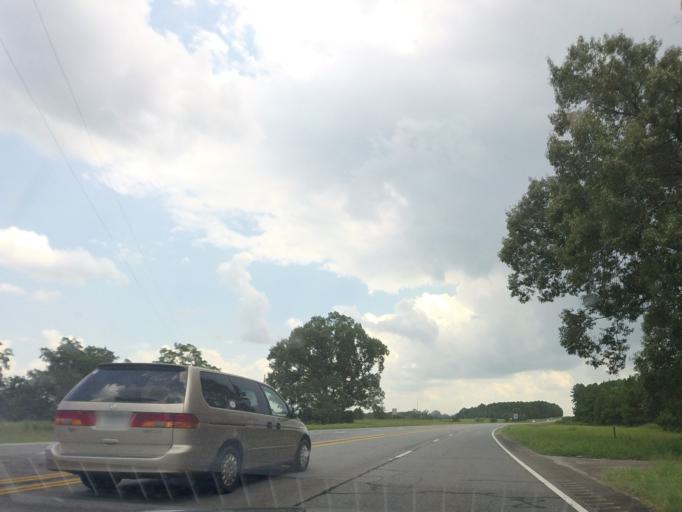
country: US
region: Georgia
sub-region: Bleckley County
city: Cochran
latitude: 32.5012
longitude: -83.4049
